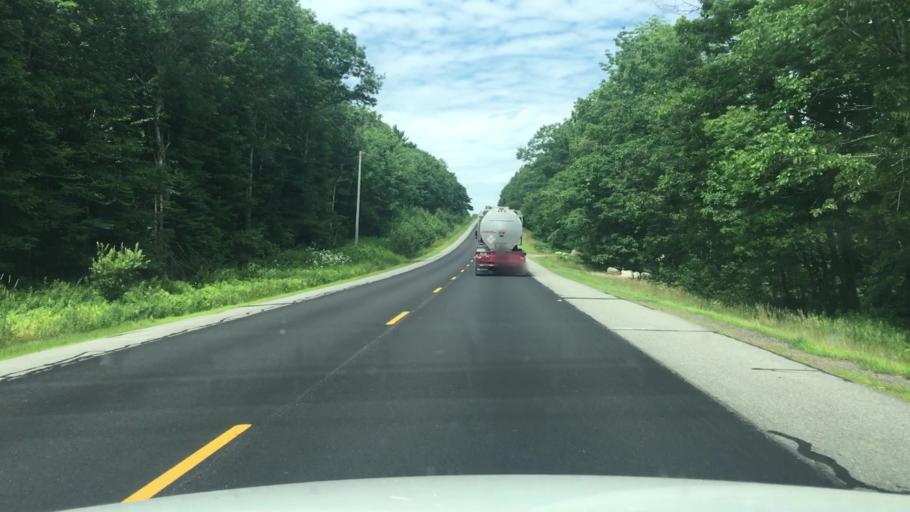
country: US
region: Maine
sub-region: Waldo County
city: Searsmont
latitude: 44.4043
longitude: -69.3001
